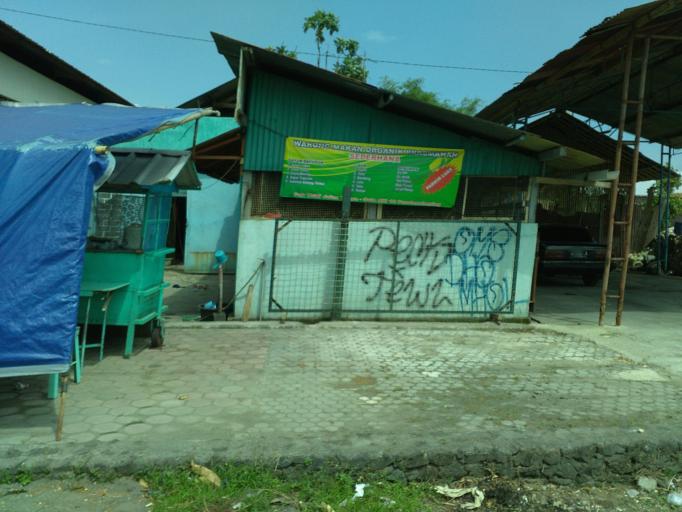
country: ID
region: Central Java
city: Candi Prambanan
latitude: -7.7418
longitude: 110.5313
